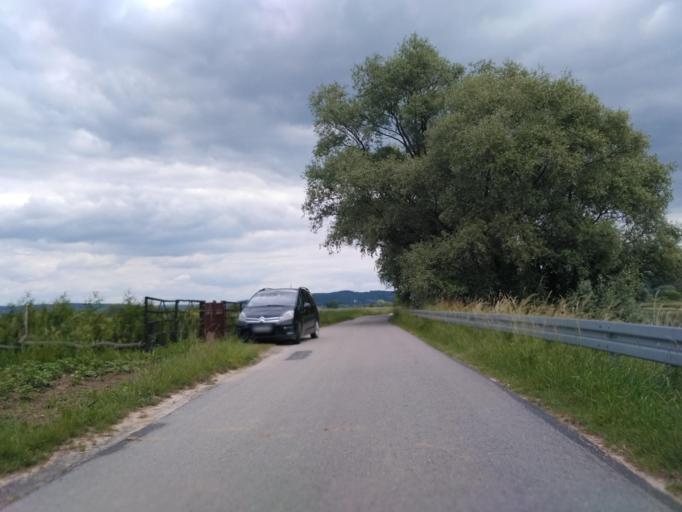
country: PL
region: Subcarpathian Voivodeship
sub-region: Powiat rzeszowski
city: Dynow
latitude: 49.8086
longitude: 22.2435
